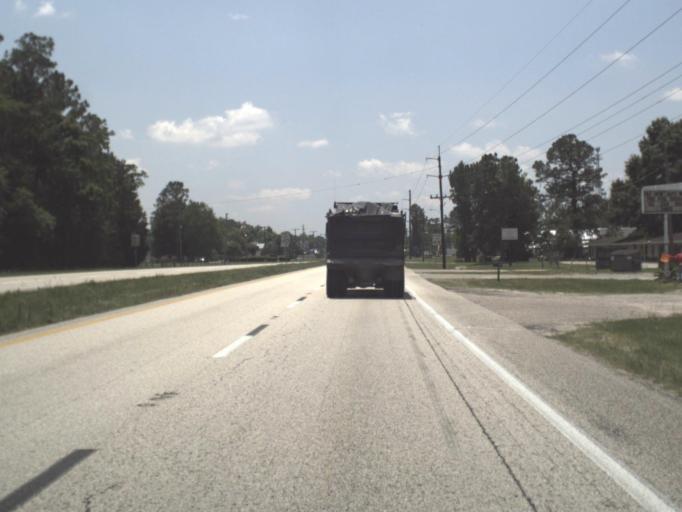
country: US
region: Florida
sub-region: Bradford County
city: Starke
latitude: 29.9707
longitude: -82.1019
